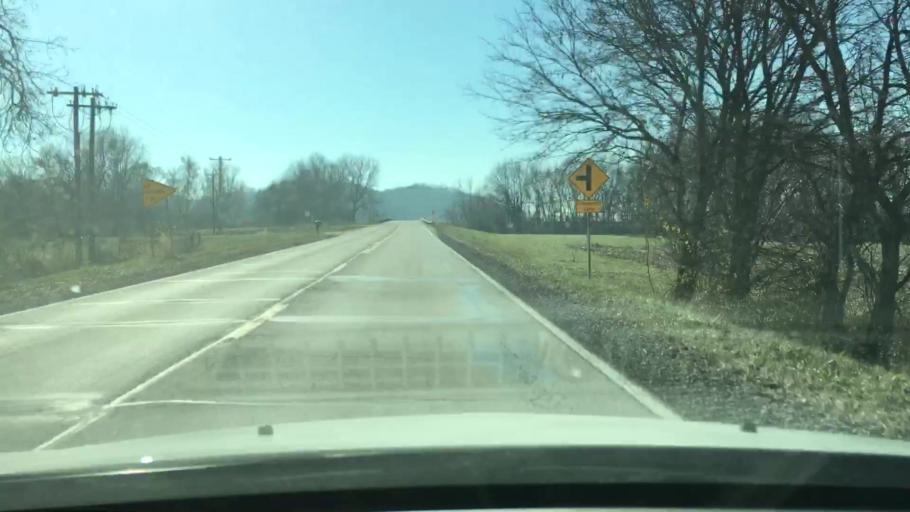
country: US
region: Illinois
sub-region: Morgan County
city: Meredosia
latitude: 39.7131
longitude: -90.5686
